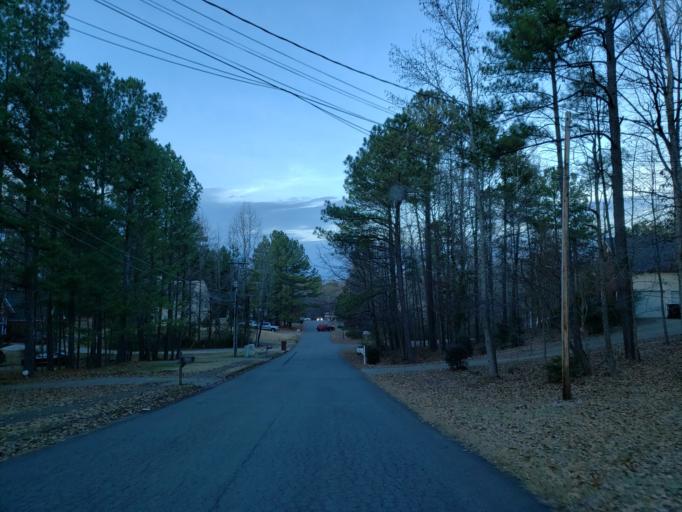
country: US
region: Georgia
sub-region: Cobb County
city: Kennesaw
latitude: 34.0452
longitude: -84.6451
